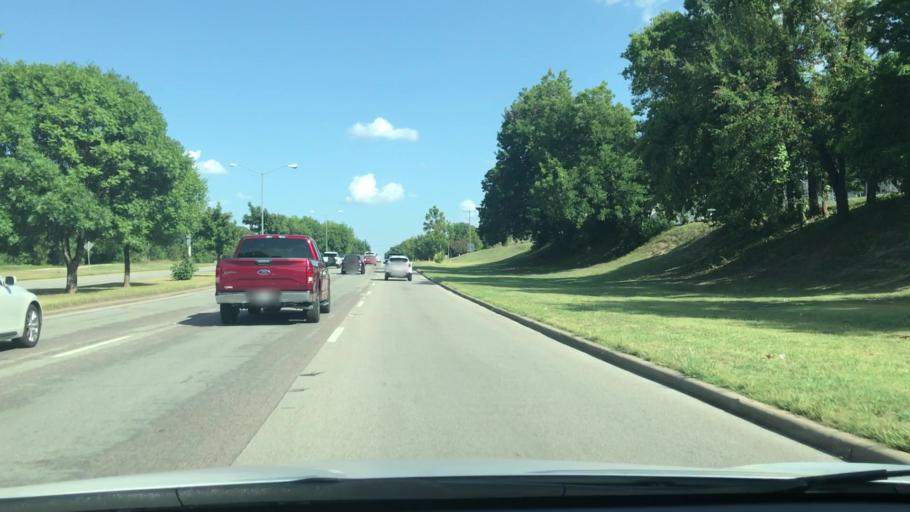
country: US
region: Texas
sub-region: Dallas County
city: University Park
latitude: 32.8581
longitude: -96.8500
